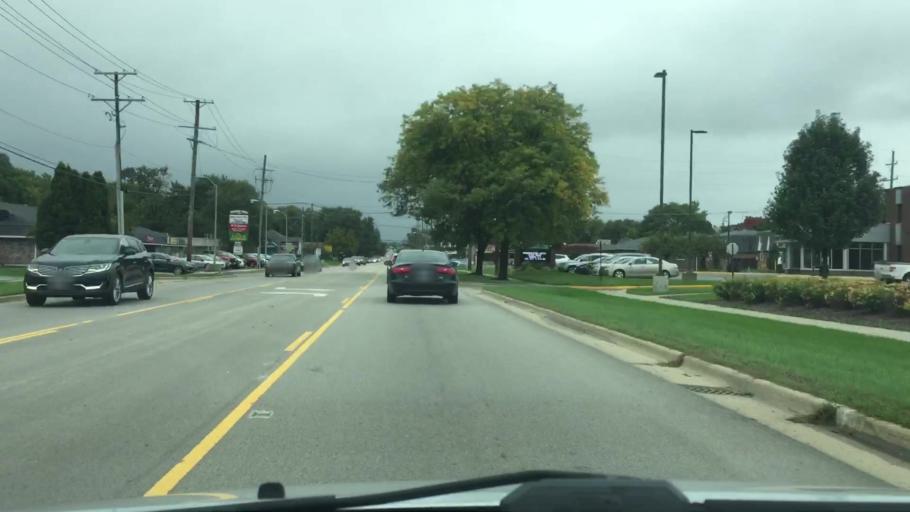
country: US
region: Illinois
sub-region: McHenry County
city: McHenry
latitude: 42.3398
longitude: -88.2747
